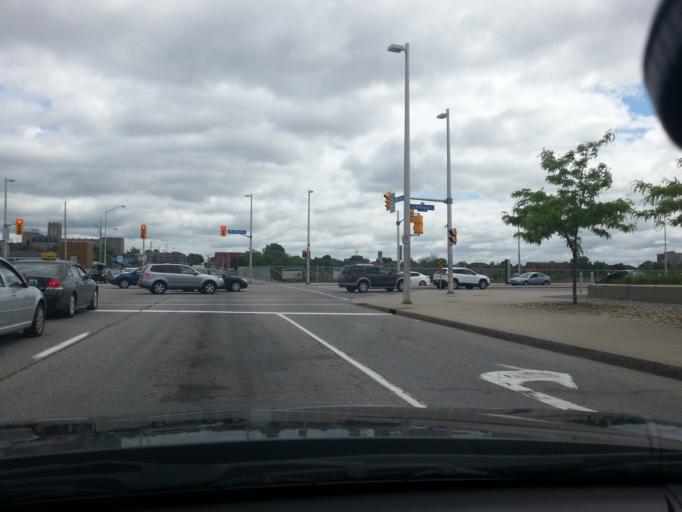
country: CA
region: Ontario
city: Ottawa
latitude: 45.4166
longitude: -75.7149
